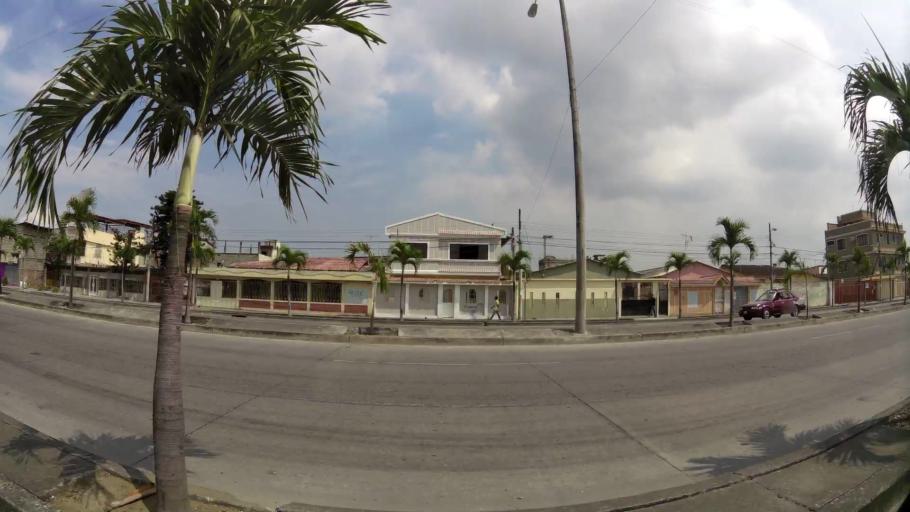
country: EC
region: Guayas
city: Guayaquil
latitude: -2.2535
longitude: -79.8897
